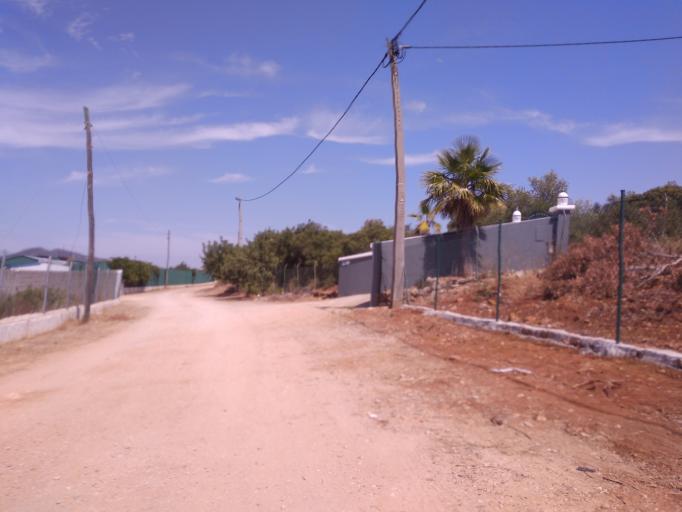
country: PT
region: Faro
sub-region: Faro
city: Santa Barbara de Nexe
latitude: 37.0922
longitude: -7.9715
